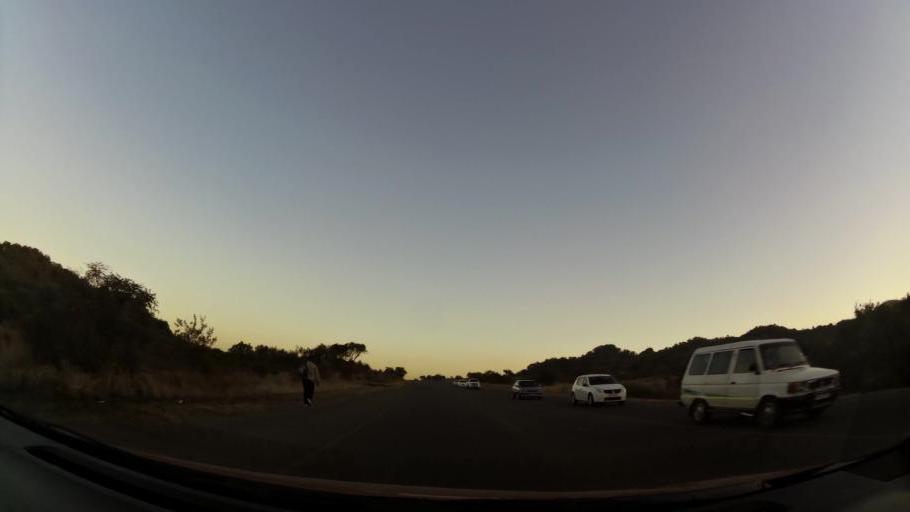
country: ZA
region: North-West
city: Ga-Rankuwa
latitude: -25.6025
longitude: 28.0395
